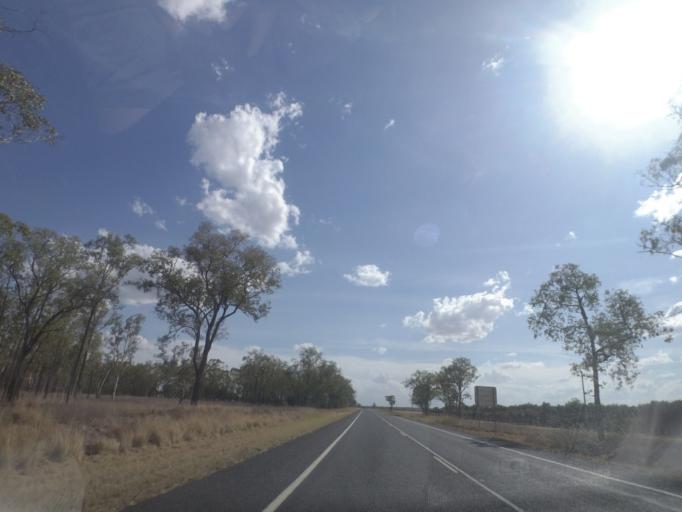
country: AU
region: New South Wales
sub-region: Moree Plains
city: Boggabilla
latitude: -28.5188
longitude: 150.9100
